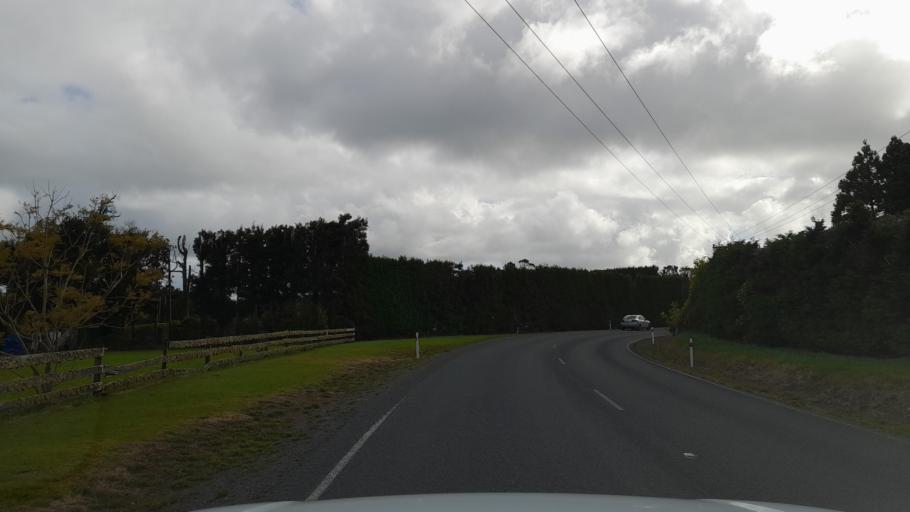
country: NZ
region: Northland
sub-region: Whangarei
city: Maungatapere
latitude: -35.7549
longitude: 174.2441
